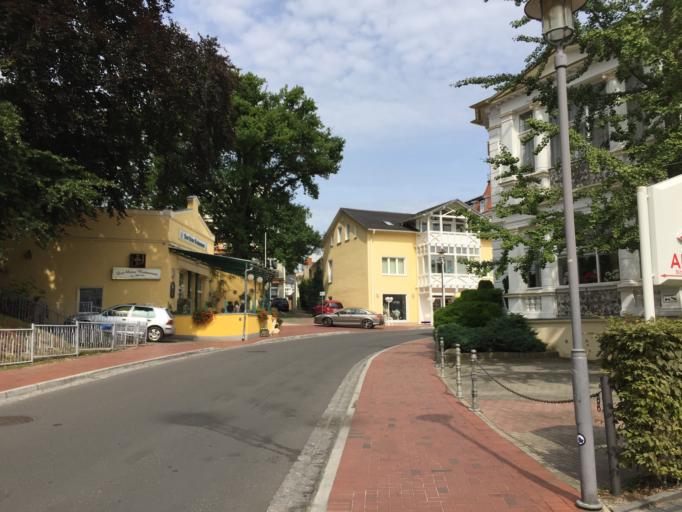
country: DE
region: Mecklenburg-Vorpommern
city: Seebad Heringsdorf
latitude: 53.9558
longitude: 14.1648
